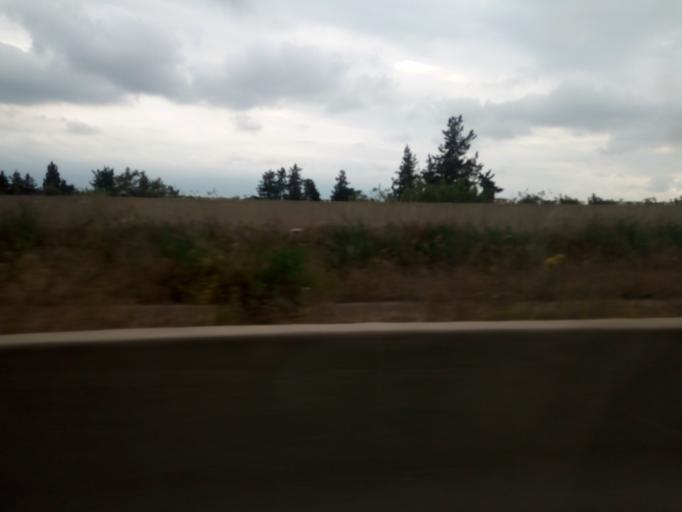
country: DZ
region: Tipaza
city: Saoula
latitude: 36.6492
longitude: 3.0180
